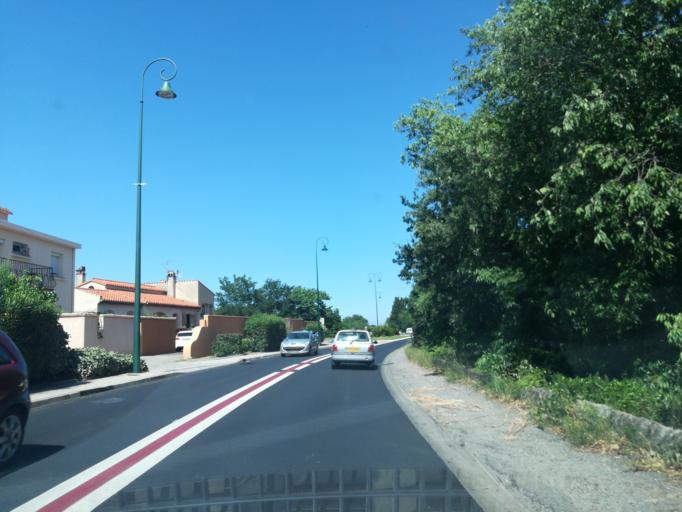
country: FR
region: Languedoc-Roussillon
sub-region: Departement des Pyrenees-Orientales
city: Ceret
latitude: 42.4991
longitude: 2.7511
